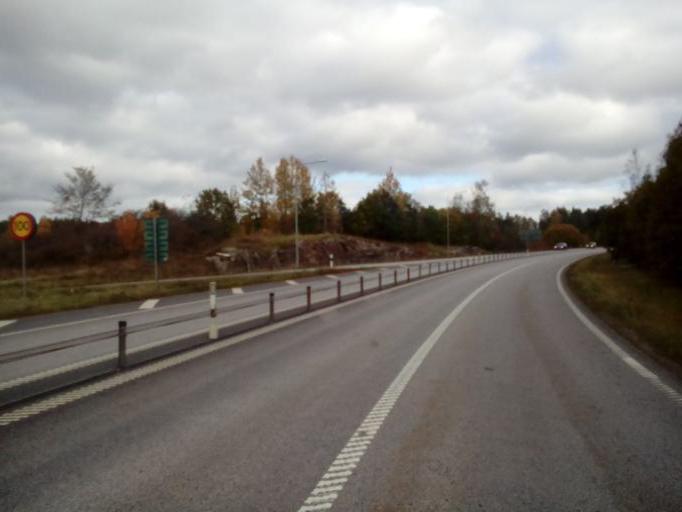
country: SE
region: Kalmar
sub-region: Vasterviks Kommun
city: Gamleby
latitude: 57.9095
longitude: 16.3867
